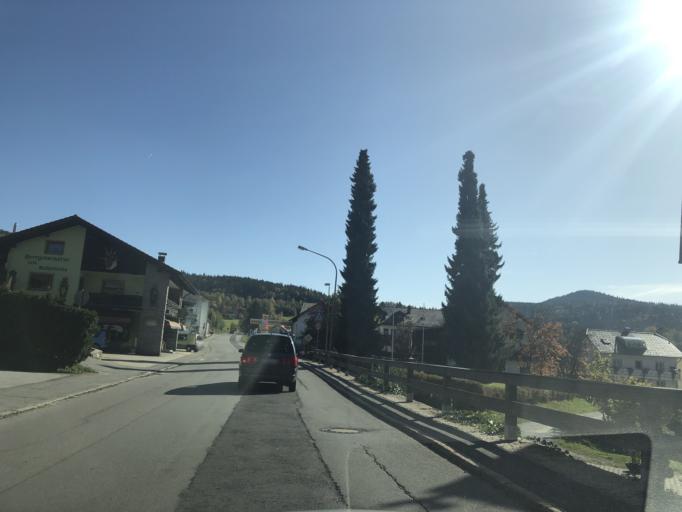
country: DE
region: Bavaria
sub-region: Lower Bavaria
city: Bodenmais
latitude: 49.0651
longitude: 13.1027
